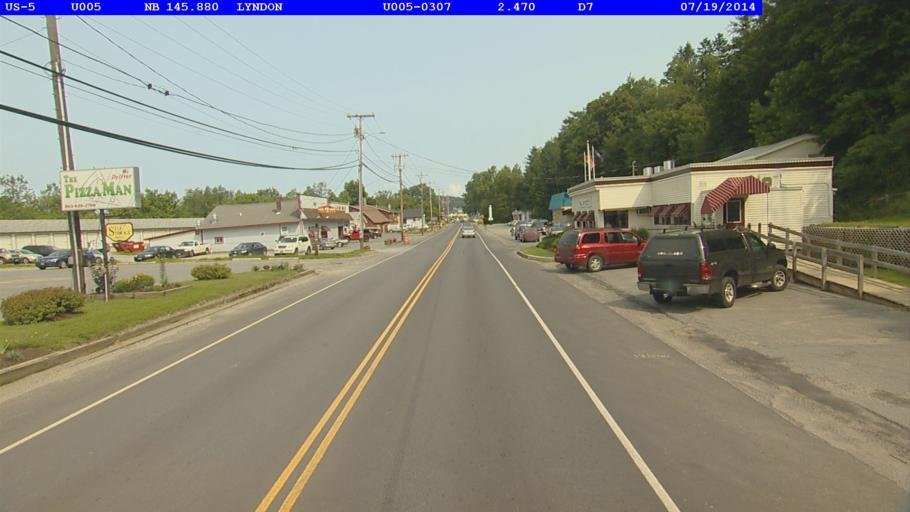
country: US
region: Vermont
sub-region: Caledonia County
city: Lyndonville
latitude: 44.5290
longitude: -72.0011
